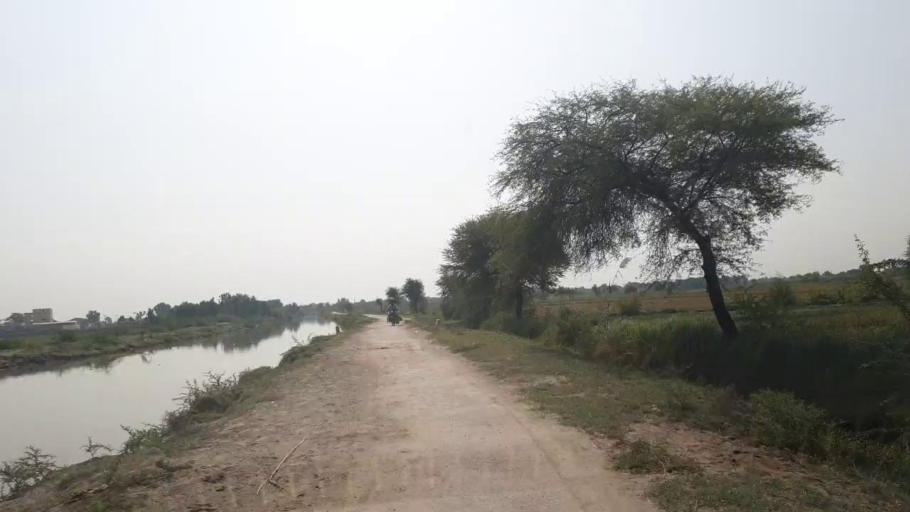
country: PK
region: Sindh
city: Badin
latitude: 24.6446
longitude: 68.8476
